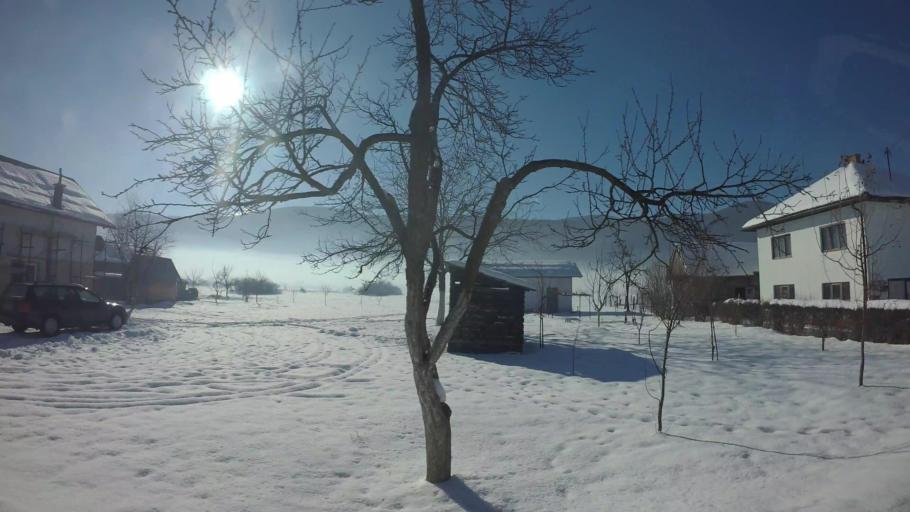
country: BA
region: Federation of Bosnia and Herzegovina
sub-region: Kanton Sarajevo
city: Sarajevo
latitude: 43.7983
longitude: 18.3370
